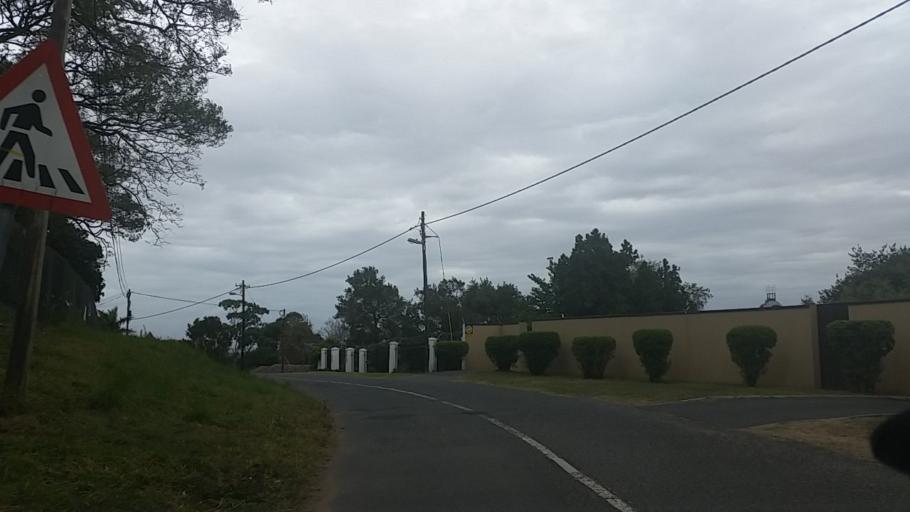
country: ZA
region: KwaZulu-Natal
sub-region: eThekwini Metropolitan Municipality
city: Berea
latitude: -29.8430
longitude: 30.9382
